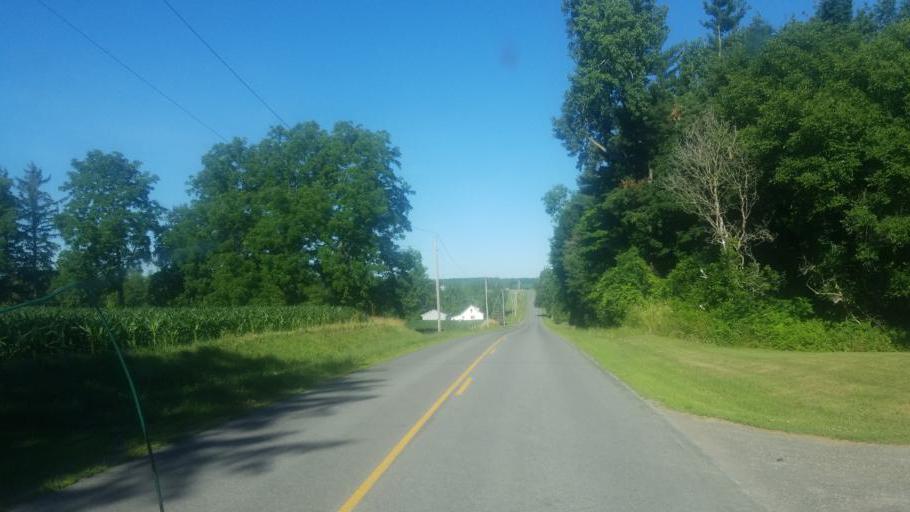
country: US
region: New York
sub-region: Ontario County
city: Clifton Springs
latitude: 42.8384
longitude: -77.1346
